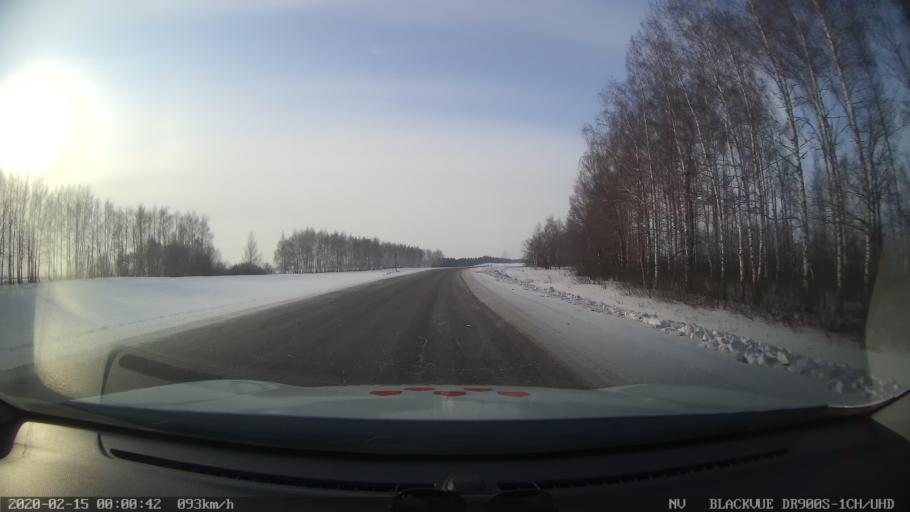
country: RU
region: Tatarstan
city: Kuybyshevskiy Zaton
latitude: 55.3439
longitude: 49.0324
